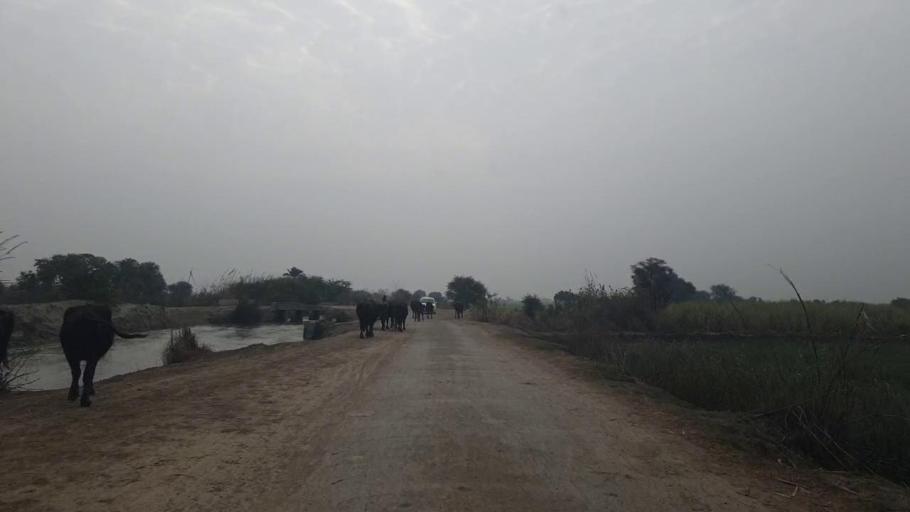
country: PK
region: Sindh
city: Tando Adam
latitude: 25.7250
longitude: 68.7262
